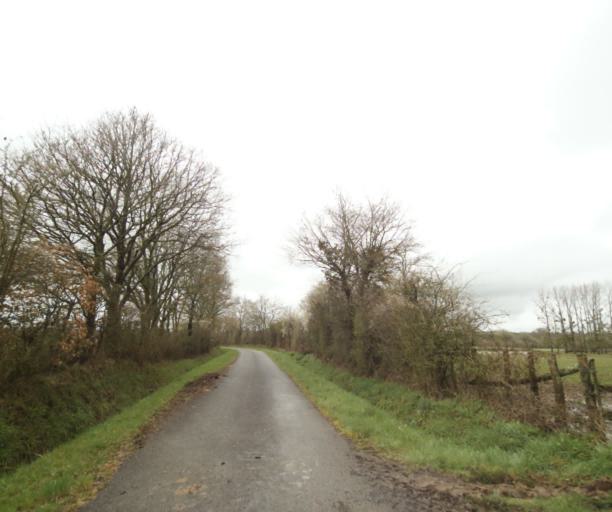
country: FR
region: Pays de la Loire
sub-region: Departement de la Loire-Atlantique
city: Quilly
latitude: 47.4565
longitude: -1.9004
